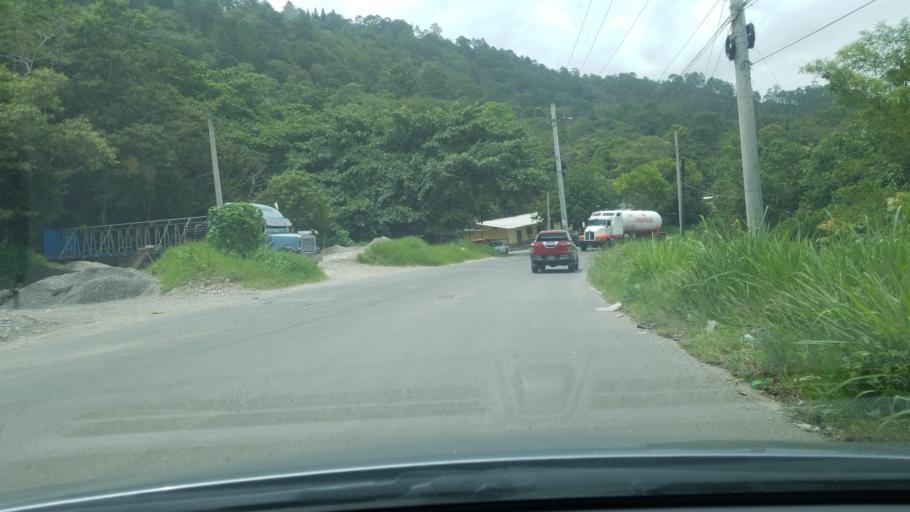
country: HN
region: Copan
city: Santa Rosa de Copan
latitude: 14.7526
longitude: -88.7739
